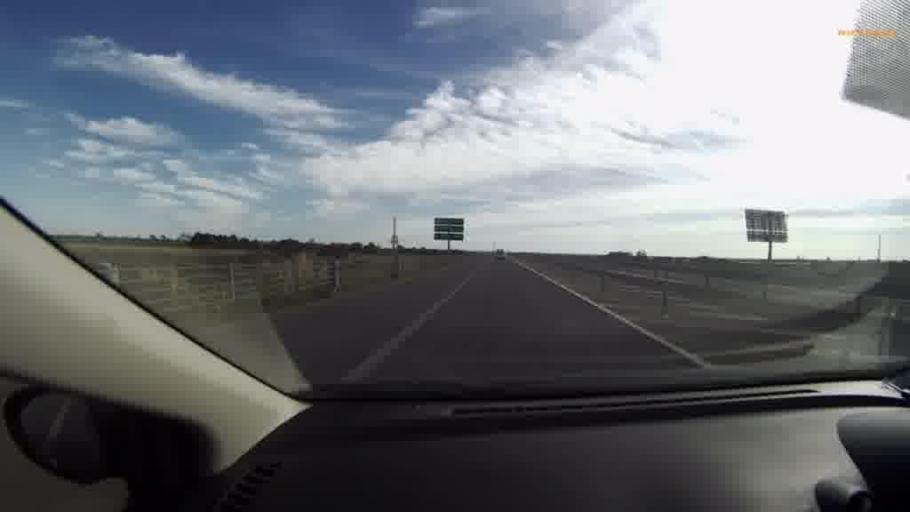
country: JP
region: Hokkaido
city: Kushiro
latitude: 43.0372
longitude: 144.3434
